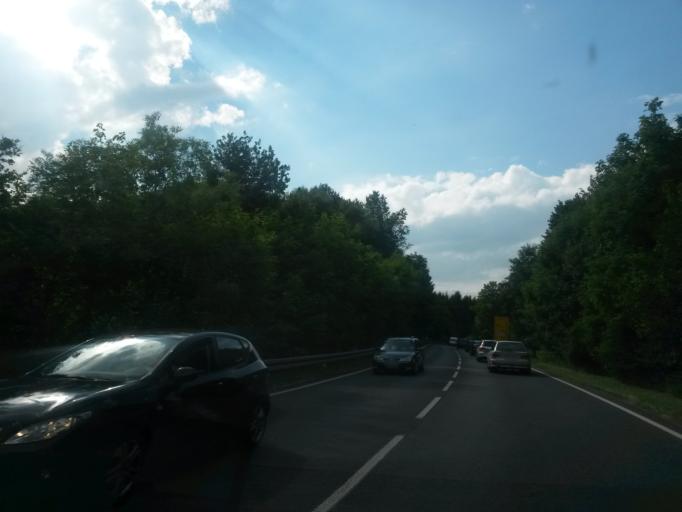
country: DE
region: Bavaria
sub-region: Upper Bavaria
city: Unterschleissheim
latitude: 48.3013
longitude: 11.5751
